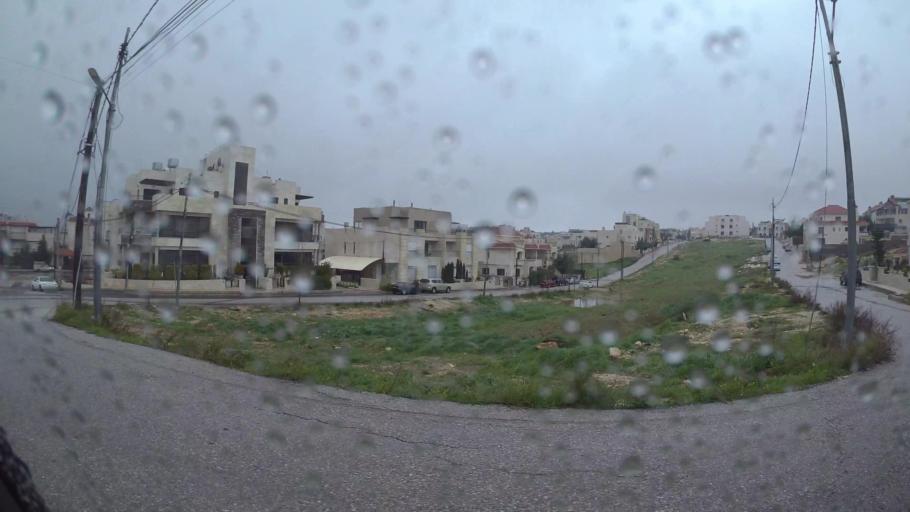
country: JO
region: Amman
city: Al Jubayhah
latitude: 32.0044
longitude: 35.8249
